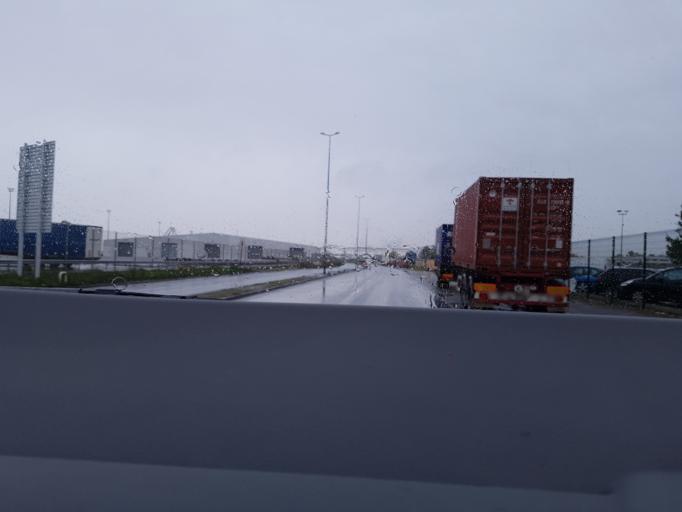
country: FR
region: Aquitaine
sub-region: Departement de la Gironde
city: Bassens
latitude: 44.8900
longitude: -0.5295
